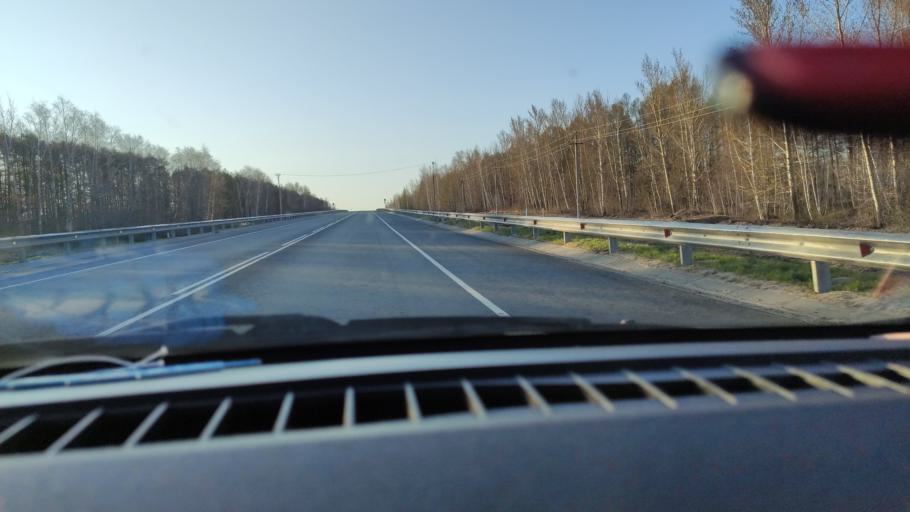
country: RU
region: Saratov
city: Shikhany
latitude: 52.1479
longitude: 47.1937
